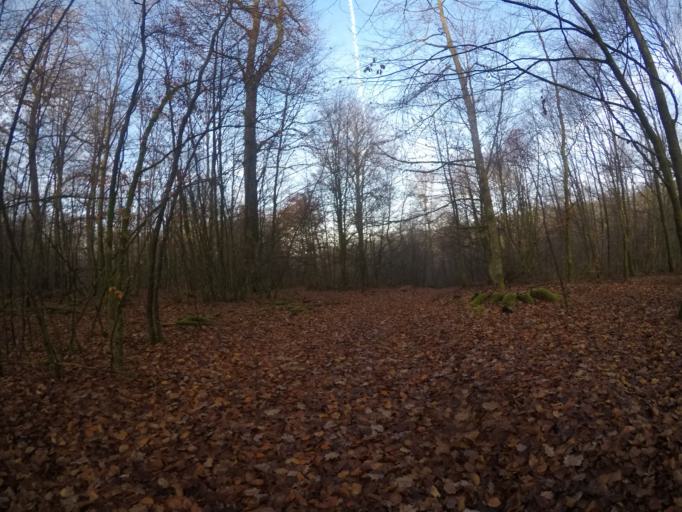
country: BE
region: Wallonia
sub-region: Province du Luxembourg
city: Habay-la-Vieille
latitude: 49.7729
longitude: 5.6609
